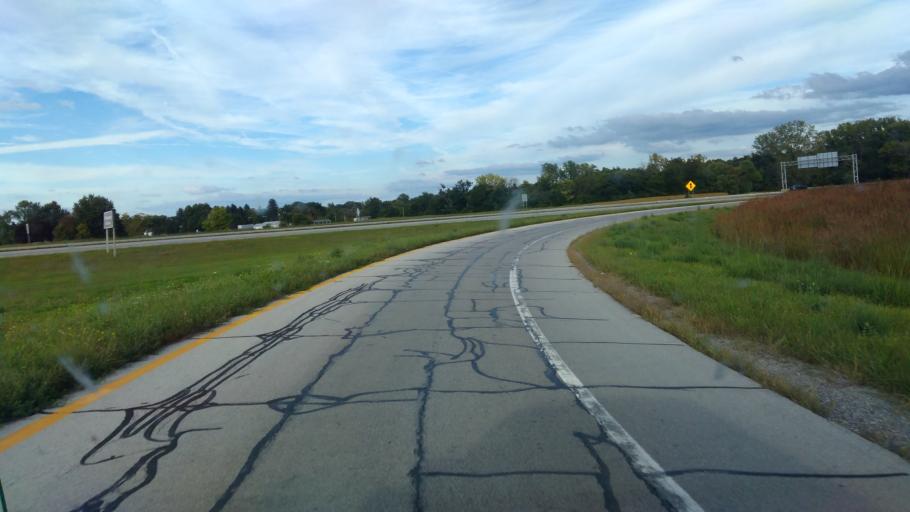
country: US
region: Ohio
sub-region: Crawford County
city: Bucyrus
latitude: 40.8239
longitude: -82.9508
